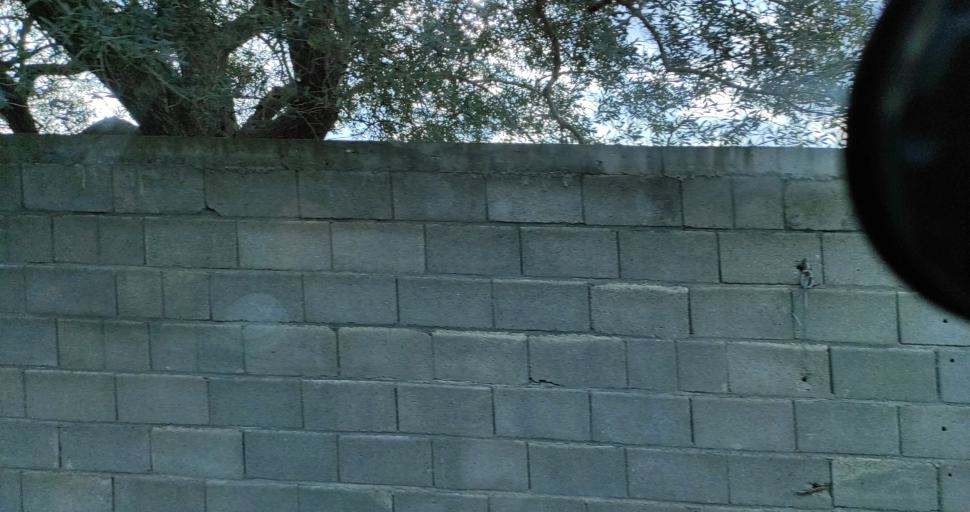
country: AL
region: Lezhe
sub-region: Rrethi i Lezhes
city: Kallmeti i Madh
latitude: 41.8798
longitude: 19.6649
